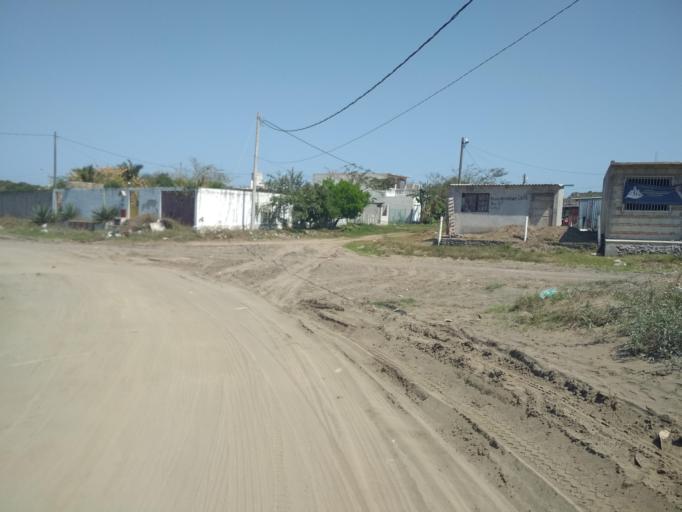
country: MX
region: Veracruz
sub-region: Veracruz
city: Lomas de Rio Medio Cuatro
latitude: 19.1889
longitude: -96.1952
